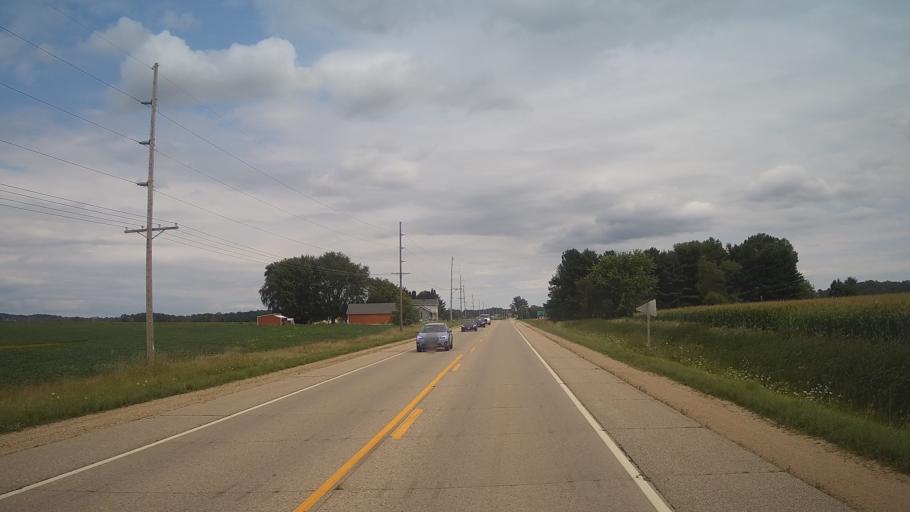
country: US
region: Wisconsin
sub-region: Waushara County
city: Redgranite
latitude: 44.0413
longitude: -89.0359
